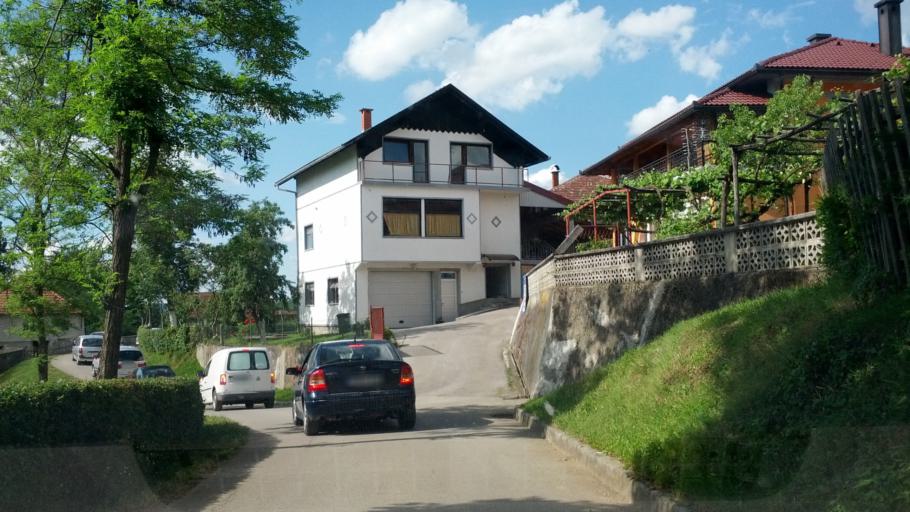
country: BA
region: Federation of Bosnia and Herzegovina
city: Ostrozac
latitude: 44.9284
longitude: 15.9561
